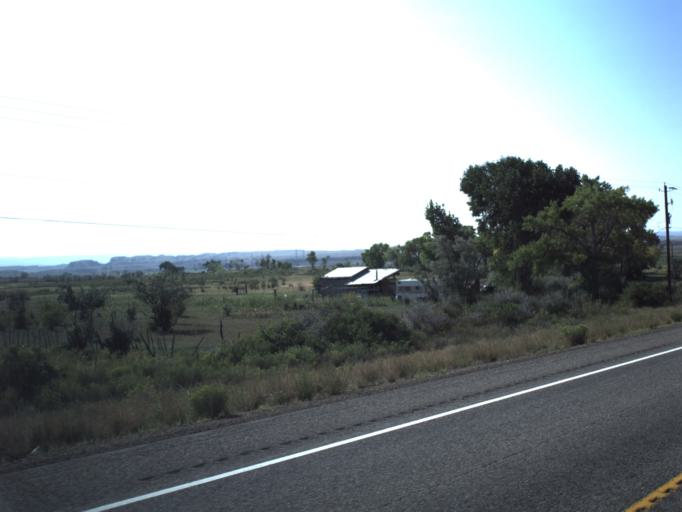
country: US
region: Utah
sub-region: Emery County
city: Castle Dale
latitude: 39.1971
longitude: -111.0242
